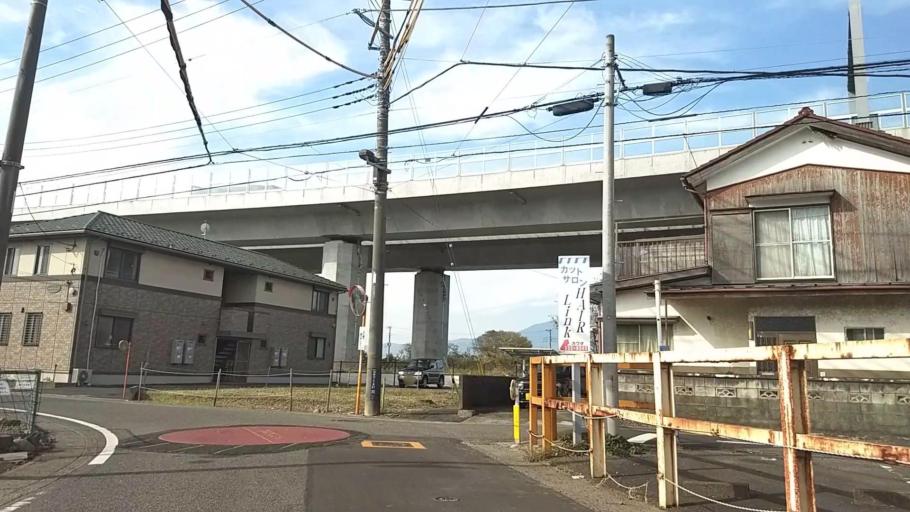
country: JP
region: Kanagawa
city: Atsugi
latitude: 35.4497
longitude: 139.3748
